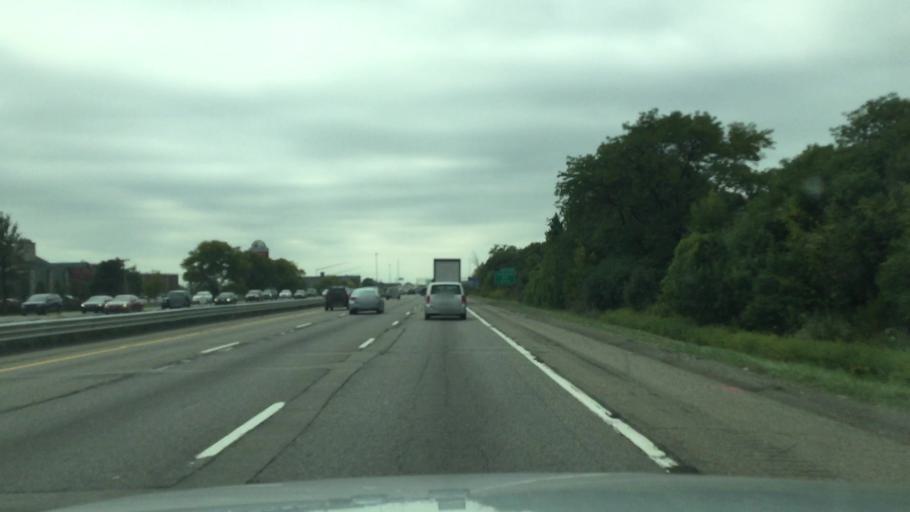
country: US
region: Michigan
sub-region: Oakland County
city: Clawson
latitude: 42.5430
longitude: -83.1167
